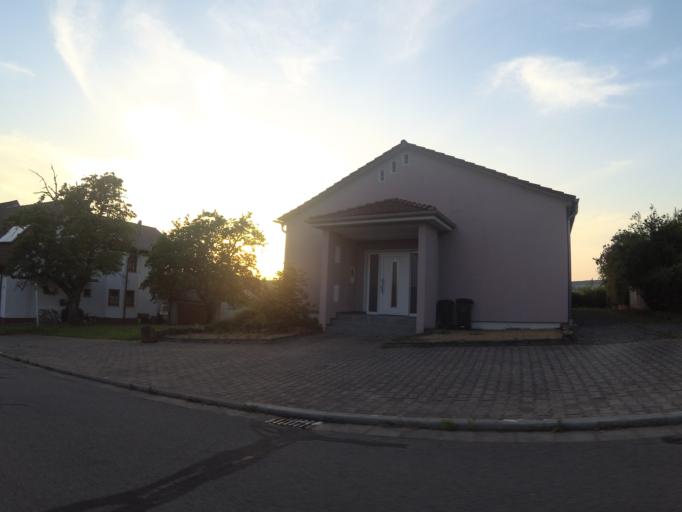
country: DE
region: Rheinland-Pfalz
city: Gries
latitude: 49.4218
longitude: 7.4000
